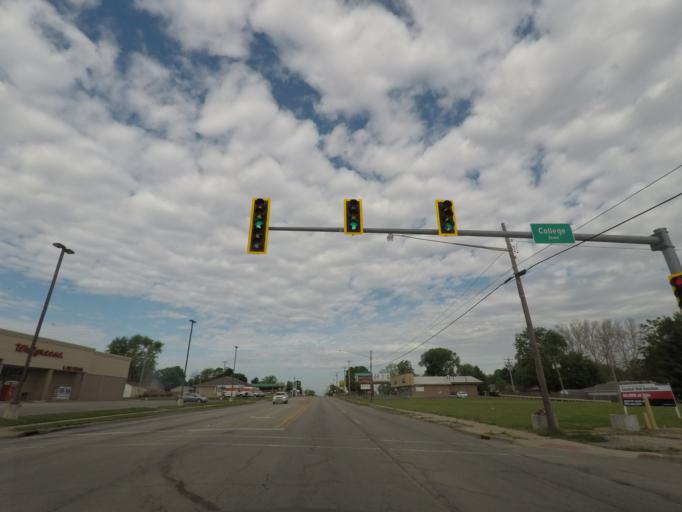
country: US
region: Illinois
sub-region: Logan County
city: Lincoln
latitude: 40.1577
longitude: -89.3751
